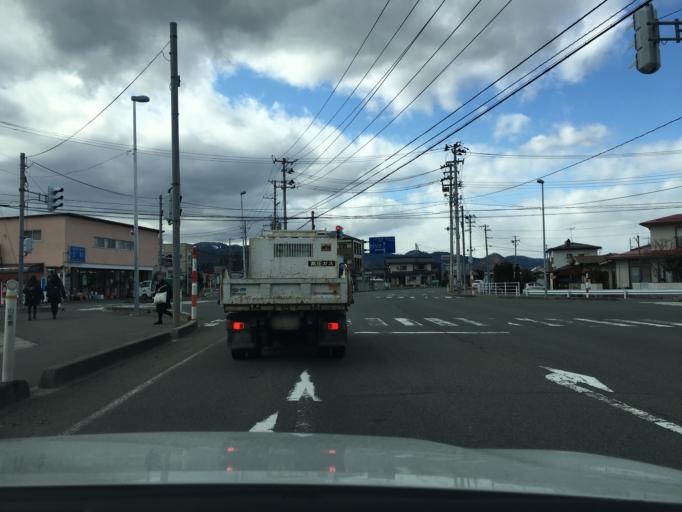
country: JP
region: Yamagata
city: Kaminoyama
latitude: 38.2052
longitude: 140.3098
